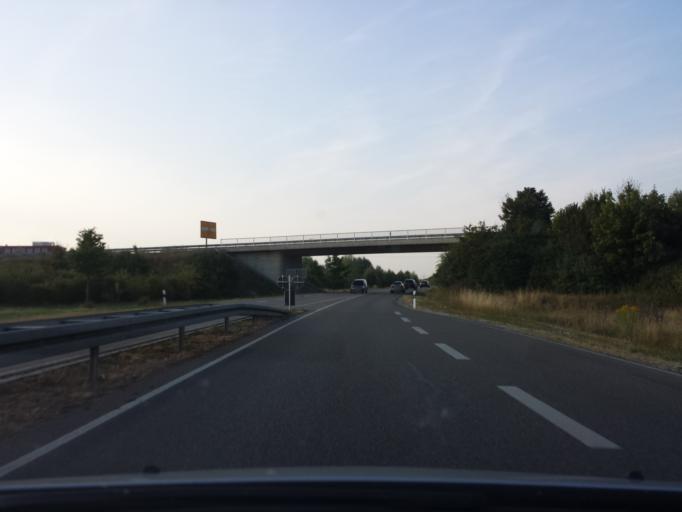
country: DE
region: Bavaria
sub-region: Swabia
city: Friedberg
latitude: 48.3629
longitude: 10.9582
